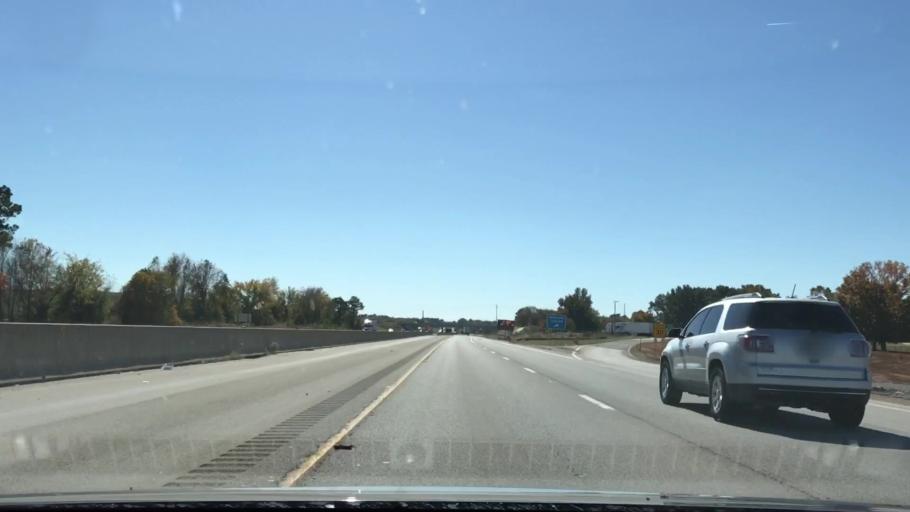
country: US
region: Tennessee
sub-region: Sumner County
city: Portland
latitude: 36.6379
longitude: -86.5717
